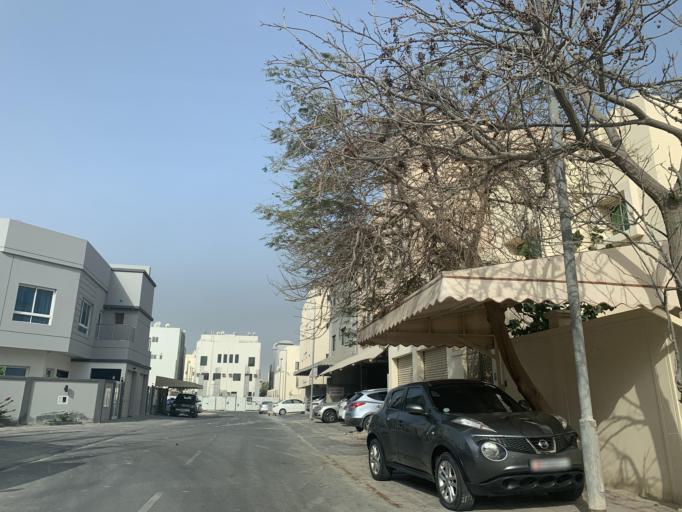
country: BH
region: Northern
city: Madinat `Isa
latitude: 26.1892
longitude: 50.5638
